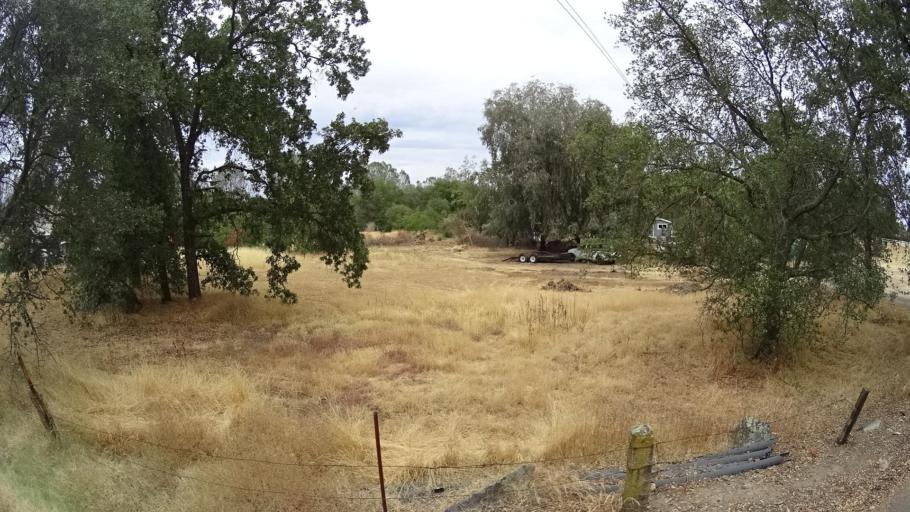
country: US
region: California
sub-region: Placer County
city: Rocklin
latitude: 38.7861
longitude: -121.2381
